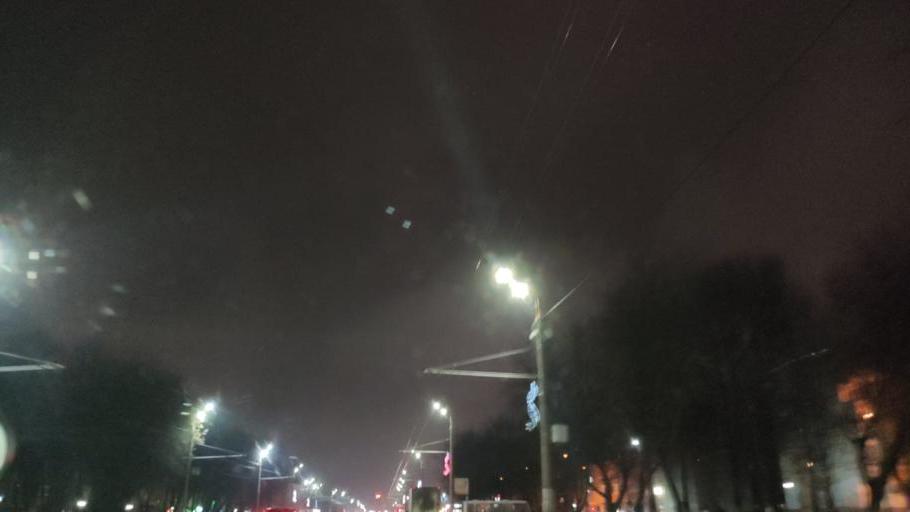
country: RU
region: Moskovskaya
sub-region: Podol'skiy Rayon
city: Podol'sk
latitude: 55.4238
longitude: 37.5220
